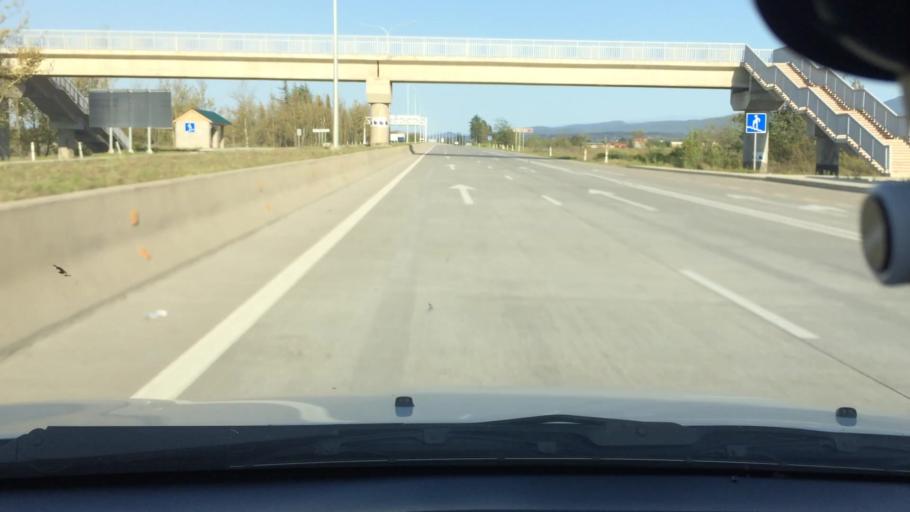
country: GE
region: Imereti
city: Zestap'oni
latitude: 42.1606
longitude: 42.9475
